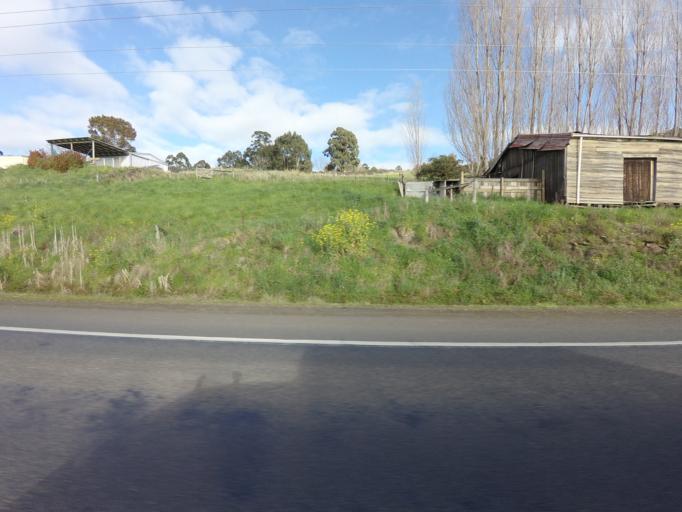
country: AU
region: Tasmania
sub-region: Huon Valley
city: Franklin
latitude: -43.1078
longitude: 147.0006
